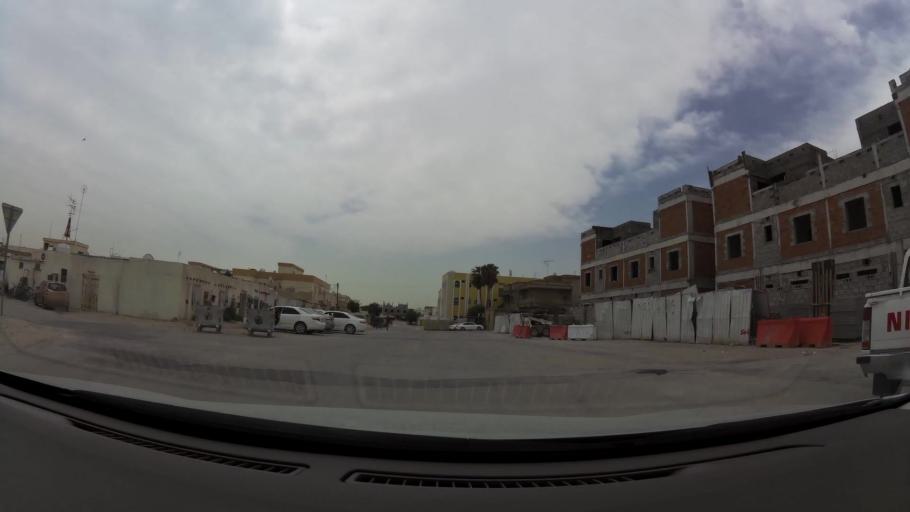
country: QA
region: Baladiyat ar Rayyan
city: Ar Rayyan
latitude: 25.2930
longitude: 51.4583
